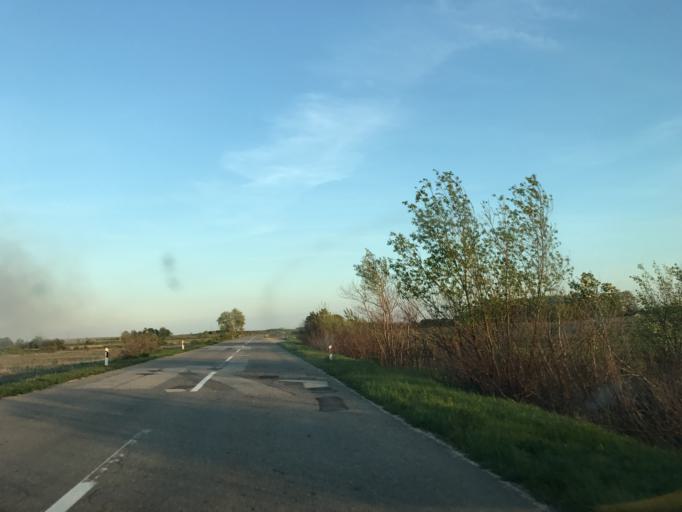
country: RO
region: Mehedinti
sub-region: Comuna Gogosu
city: Ostrovu Mare
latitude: 44.3853
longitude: 22.4734
